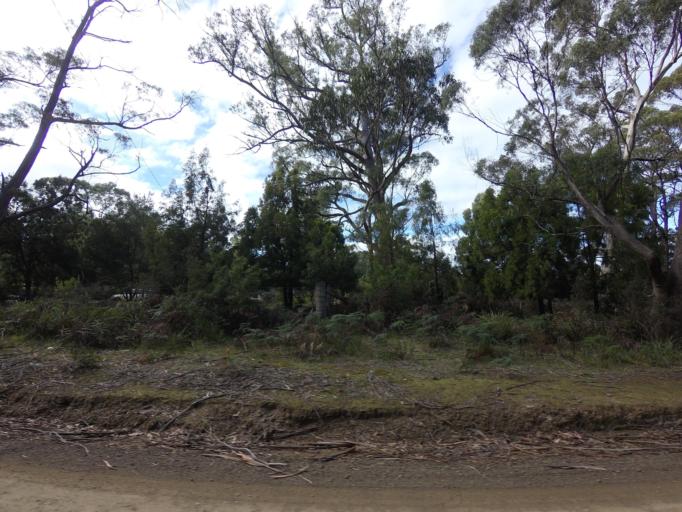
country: AU
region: Tasmania
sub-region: Clarence
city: Sandford
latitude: -43.0916
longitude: 147.7145
